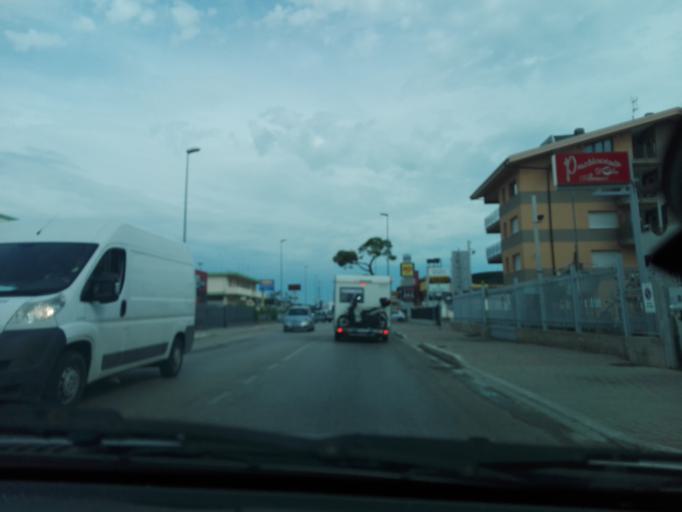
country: IT
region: Abruzzo
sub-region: Provincia di Teramo
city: Silvi
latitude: 42.5392
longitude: 14.1258
